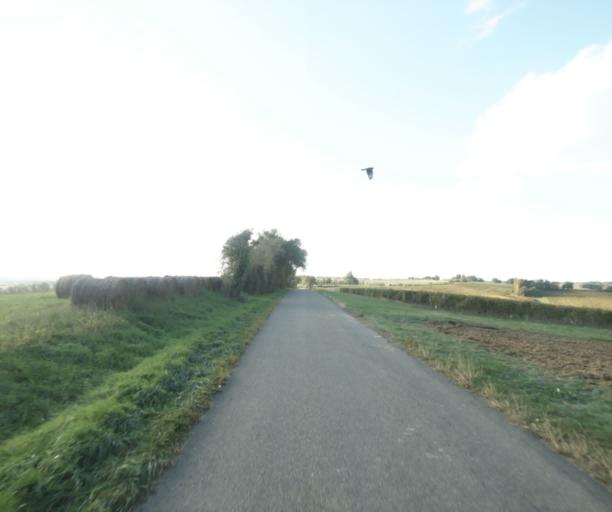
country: FR
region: Midi-Pyrenees
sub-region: Departement du Gers
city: Eauze
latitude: 43.7410
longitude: 0.1408
